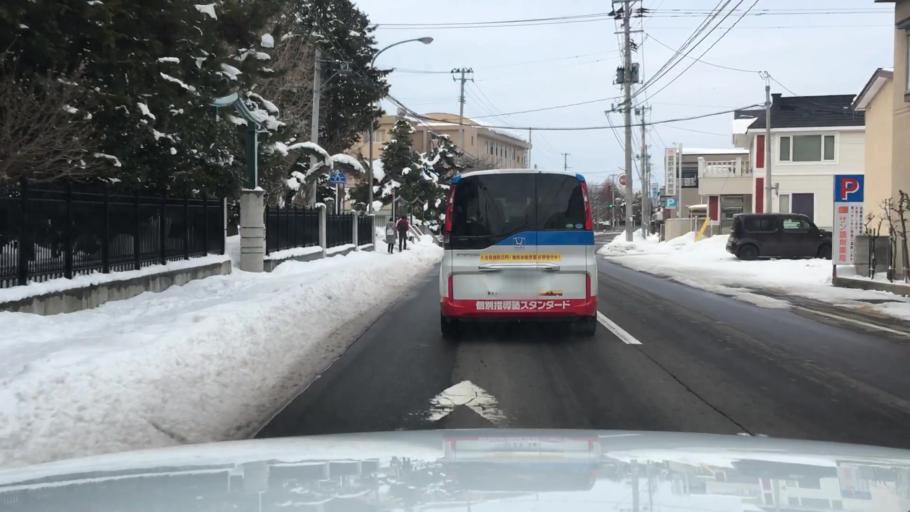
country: JP
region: Aomori
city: Hirosaki
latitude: 40.5881
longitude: 140.4744
